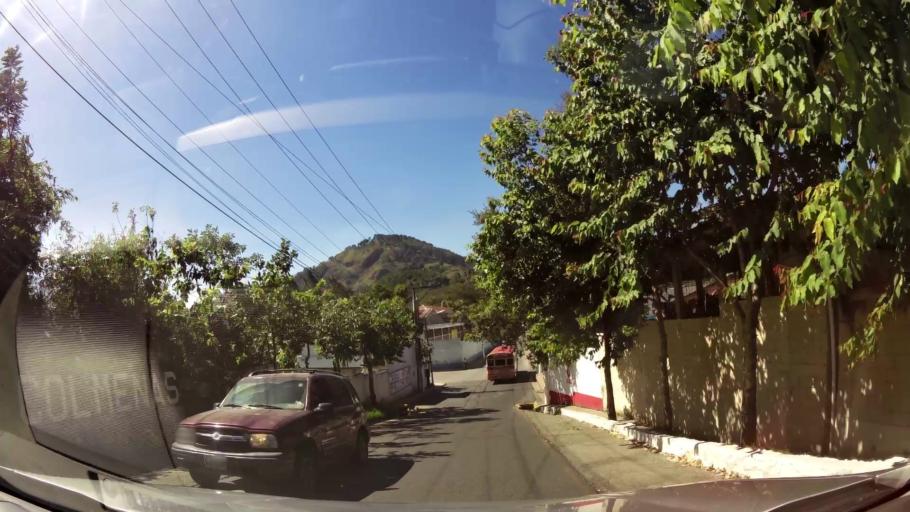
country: GT
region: Guatemala
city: Villa Canales
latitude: 14.4817
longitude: -90.5323
